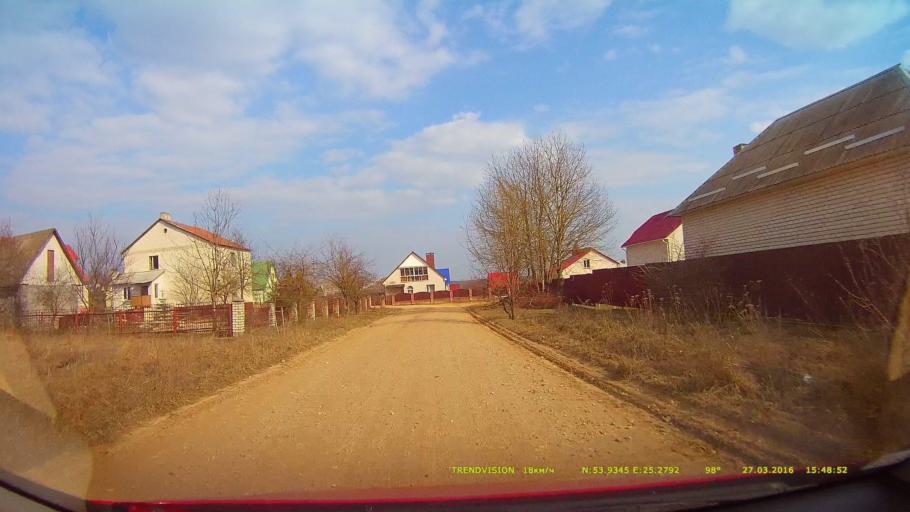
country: BY
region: Grodnenskaya
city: Lida
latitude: 53.9348
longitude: 25.2797
